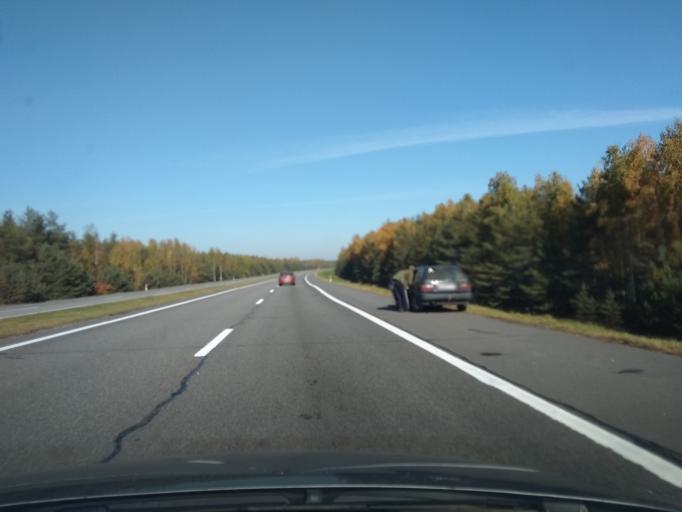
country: BY
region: Grodnenskaya
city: Zhyrovichy
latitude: 52.9178
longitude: 25.6855
